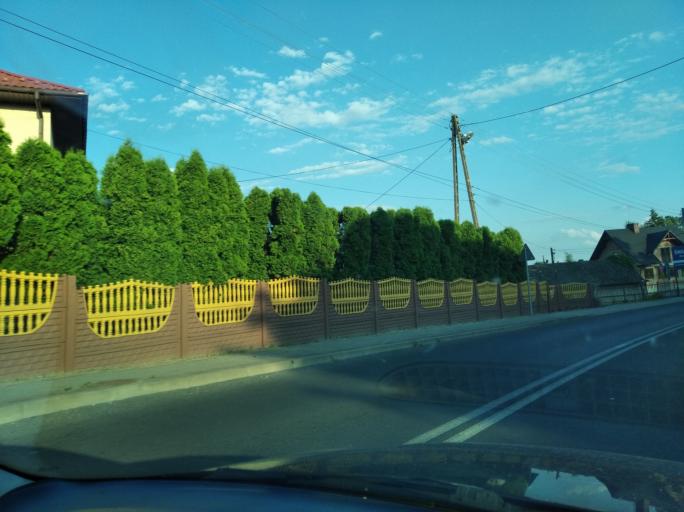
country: PL
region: Subcarpathian Voivodeship
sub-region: Powiat lezajski
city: Stare Miasto
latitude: 50.2830
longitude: 22.4303
